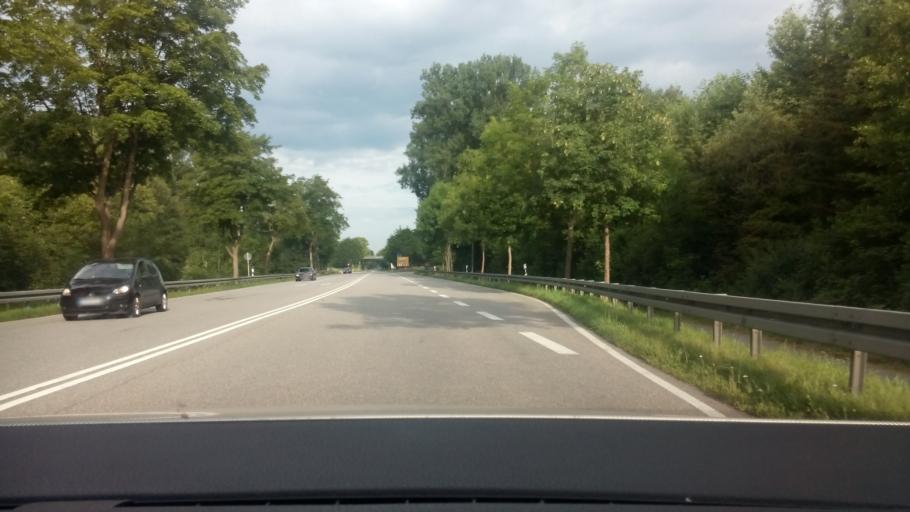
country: DE
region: Bavaria
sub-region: Upper Bavaria
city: Hebertshausen
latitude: 48.2541
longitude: 11.5030
